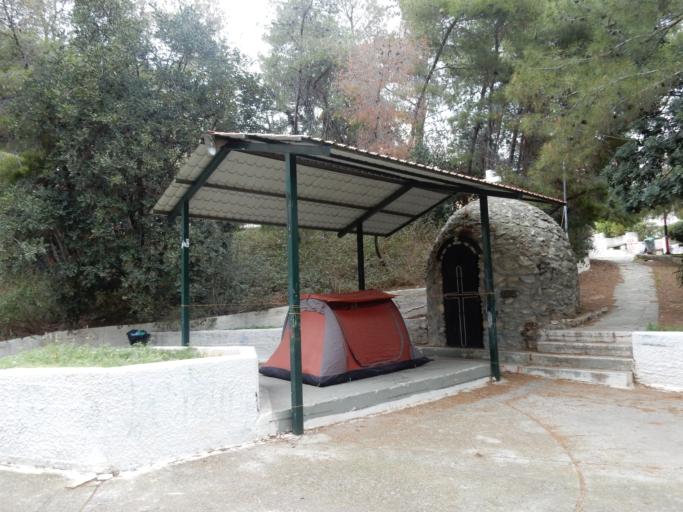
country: GR
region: Attica
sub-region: Nomos Piraios
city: Perama
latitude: 37.9683
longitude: 23.5639
